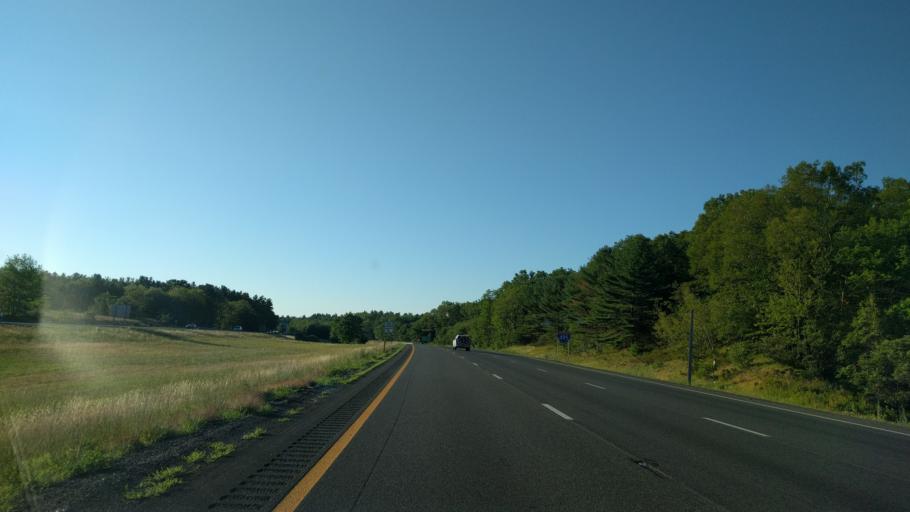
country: US
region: Massachusetts
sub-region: Norfolk County
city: Bellingham
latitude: 42.1103
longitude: -71.4627
